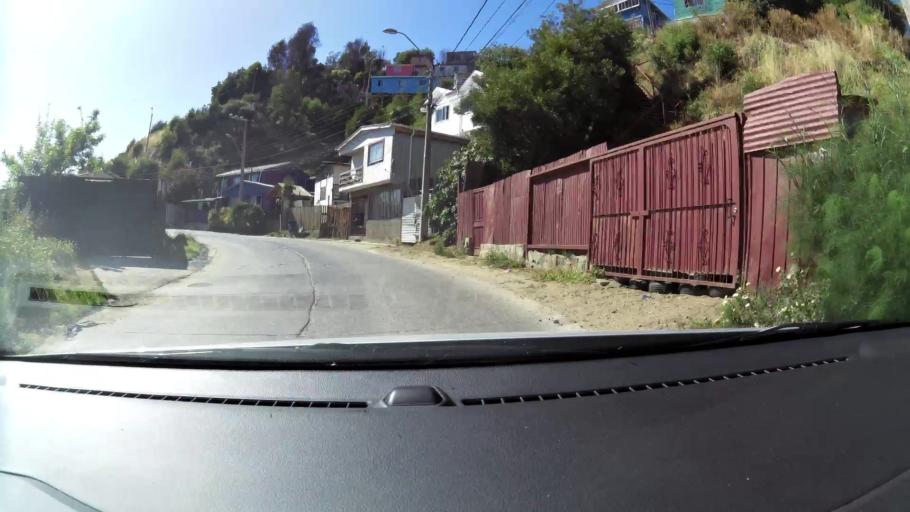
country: CL
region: Valparaiso
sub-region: Provincia de Valparaiso
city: Valparaiso
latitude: -33.0692
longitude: -71.5888
